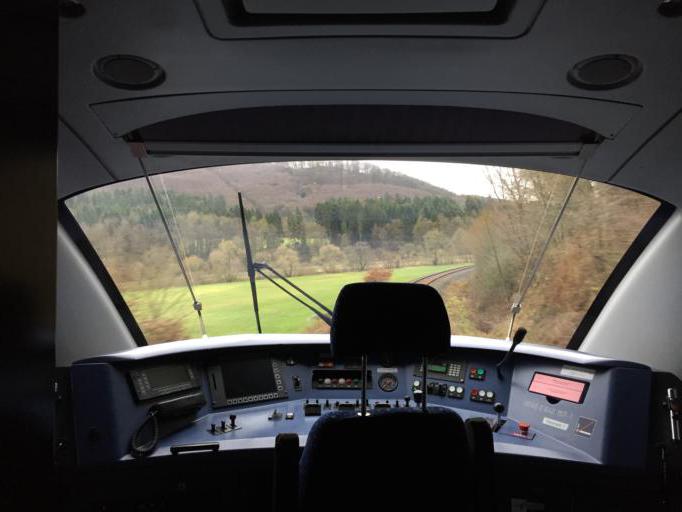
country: DE
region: Hesse
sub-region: Regierungsbezirk Kassel
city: Frankenau
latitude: 51.1172
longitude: 8.8726
